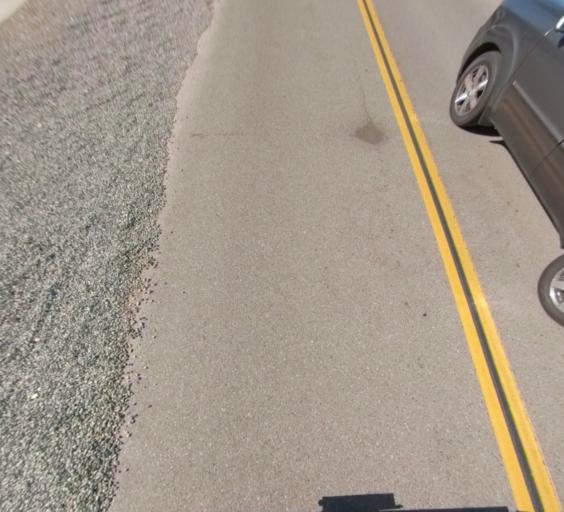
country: US
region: California
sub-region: Madera County
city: Bonadelle Ranchos-Madera Ranchos
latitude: 36.8964
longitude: -119.7981
